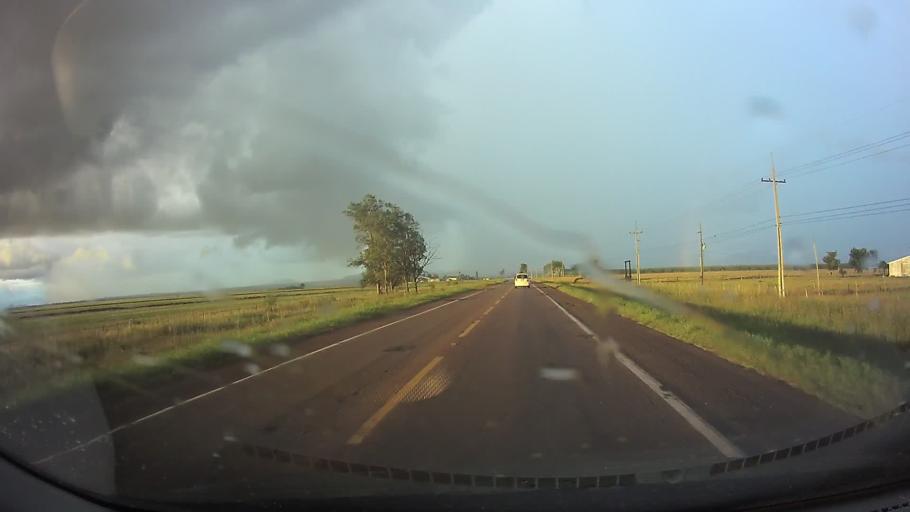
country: PY
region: Paraguari
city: Paraguari
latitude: -25.6855
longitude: -57.1680
